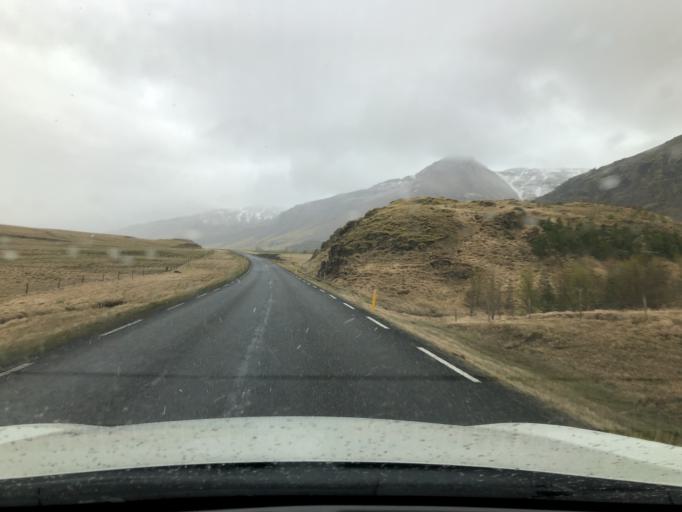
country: IS
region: East
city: Hoefn
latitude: 64.3433
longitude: -15.2467
